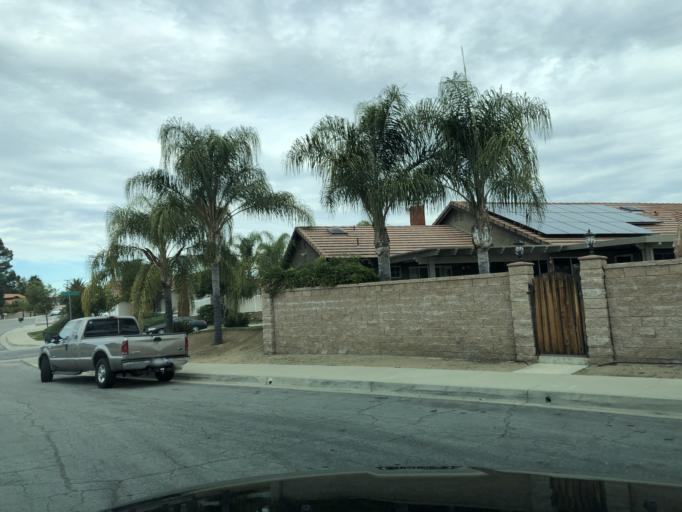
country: US
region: California
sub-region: Riverside County
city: Wildomar
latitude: 33.6219
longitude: -117.2719
